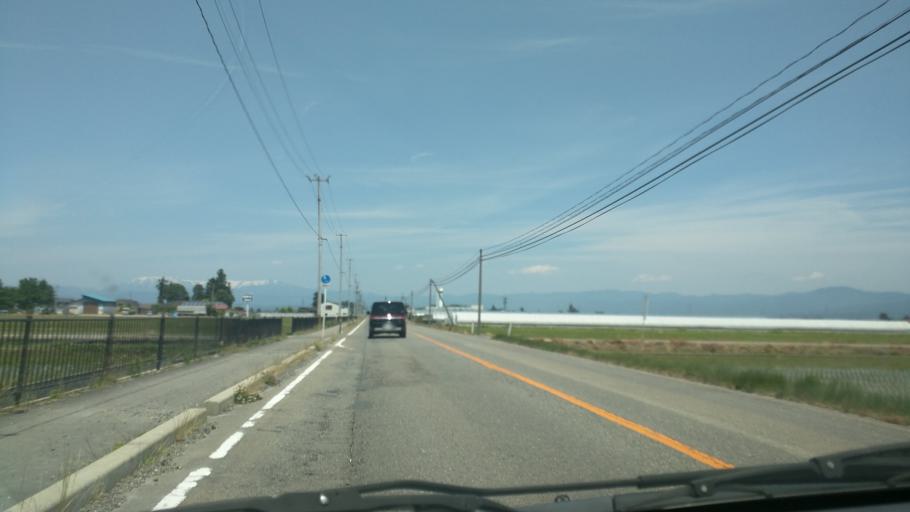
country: JP
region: Fukushima
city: Kitakata
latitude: 37.4831
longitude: 139.8751
